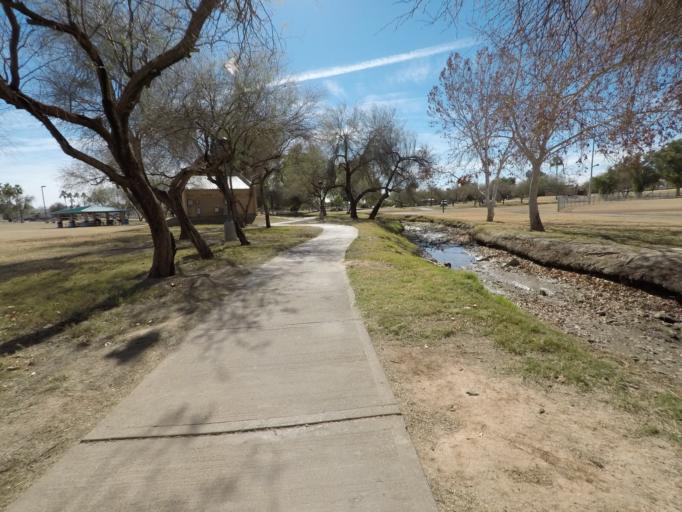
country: US
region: Arizona
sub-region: Maricopa County
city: Scottsdale
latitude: 33.4704
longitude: -111.9155
